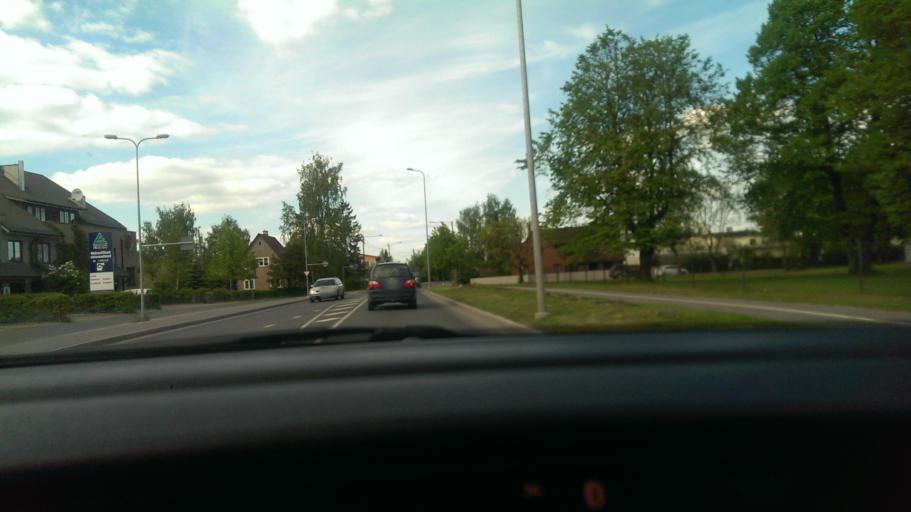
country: EE
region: Tartu
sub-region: UElenurme vald
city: Ulenurme
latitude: 58.3459
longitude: 26.7151
